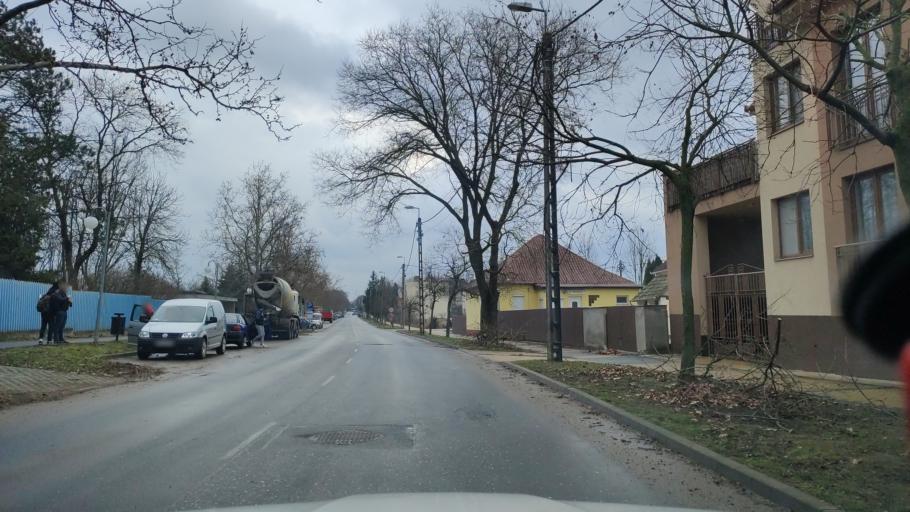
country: HU
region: Hajdu-Bihar
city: Hajduszoboszlo
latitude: 47.4532
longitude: 21.3936
